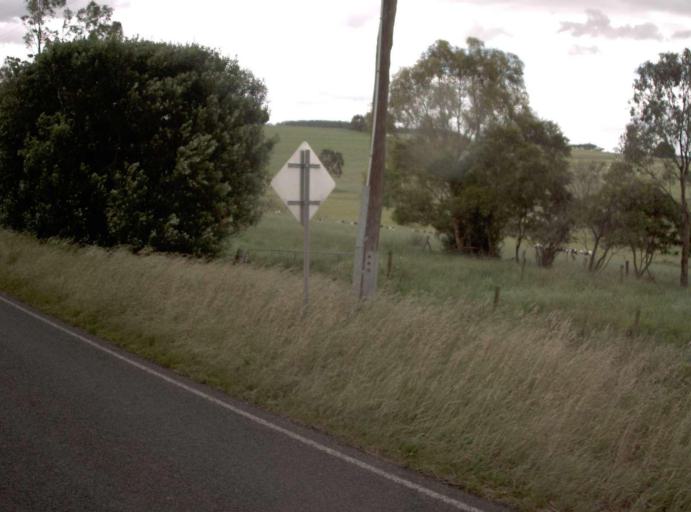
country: AU
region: Victoria
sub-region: Baw Baw
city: Warragul
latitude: -38.1441
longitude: 145.9867
